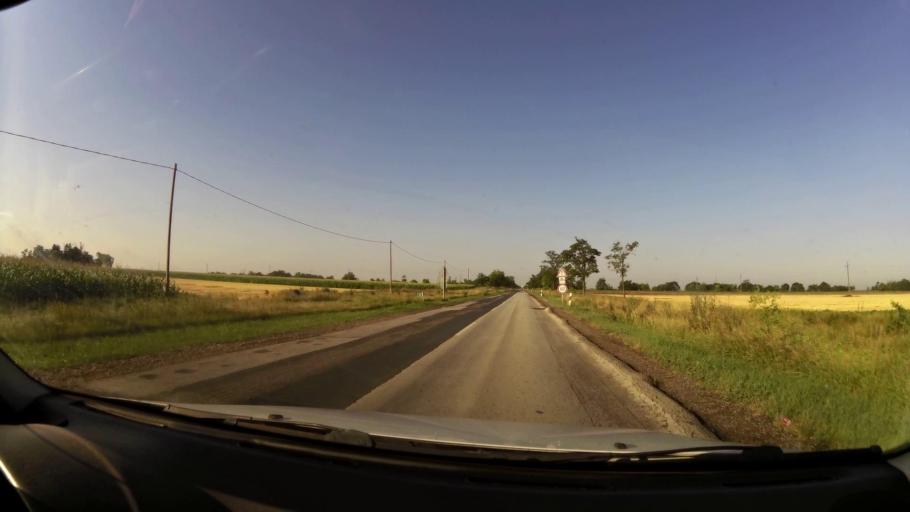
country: HU
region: Pest
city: Cegled
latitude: 47.2163
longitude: 19.8260
